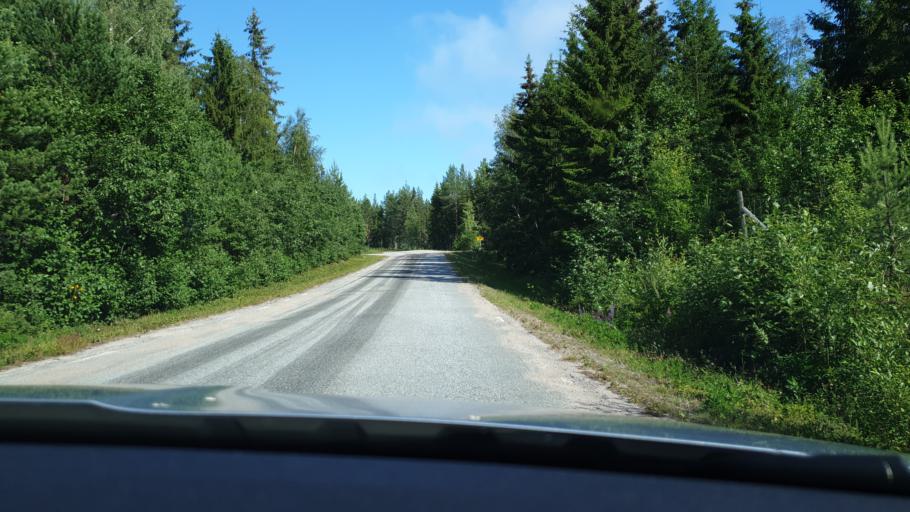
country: SE
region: Gaevleborg
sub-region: Soderhamns Kommun
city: Soderhamn
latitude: 61.4277
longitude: 16.9875
